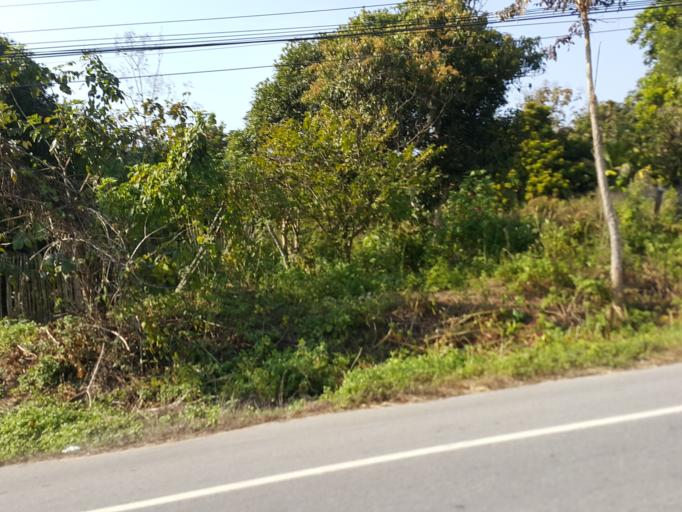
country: TH
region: Lampang
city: Chae Hom
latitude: 18.6660
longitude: 99.5466
